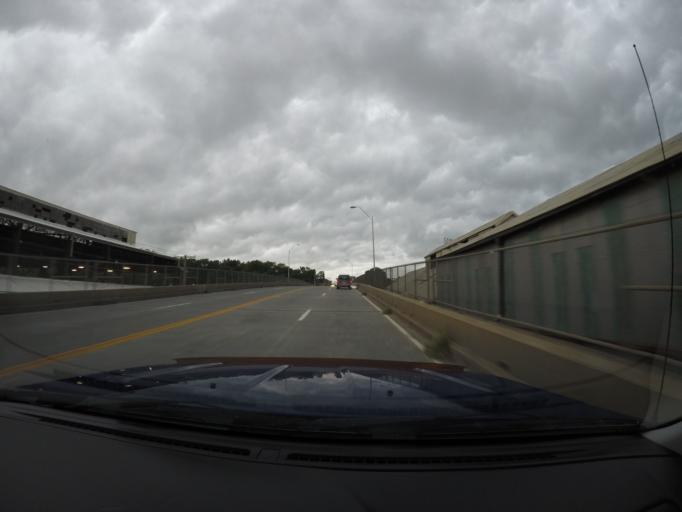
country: US
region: Missouri
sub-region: Jackson County
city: Sugar Creek
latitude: 39.1045
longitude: -94.4991
